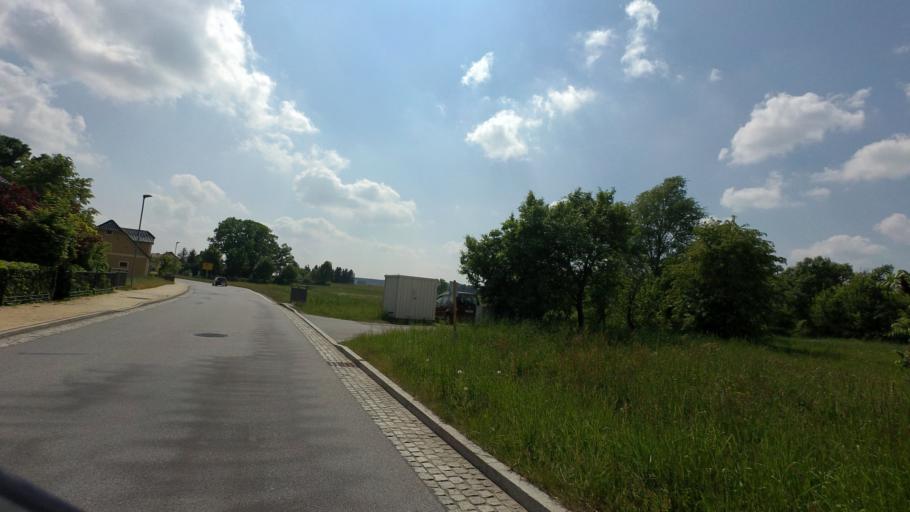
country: DE
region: Saxony
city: Mucka
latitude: 51.2702
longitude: 14.6466
